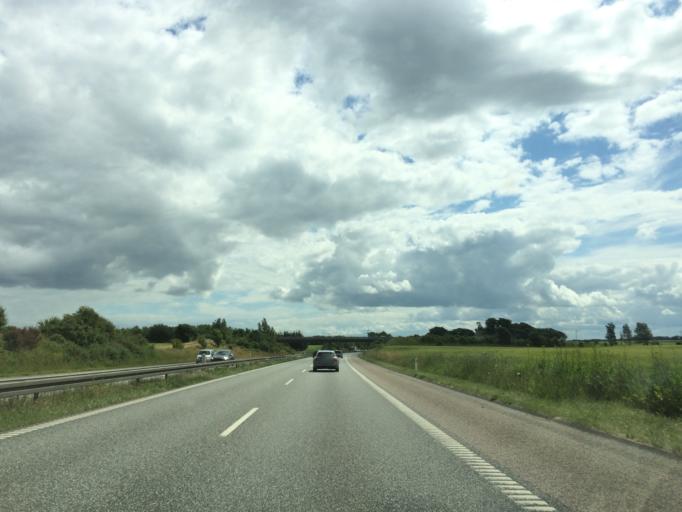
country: DK
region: North Denmark
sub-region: Mariagerfjord Kommune
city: Hobro
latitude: 56.7148
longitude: 9.7254
